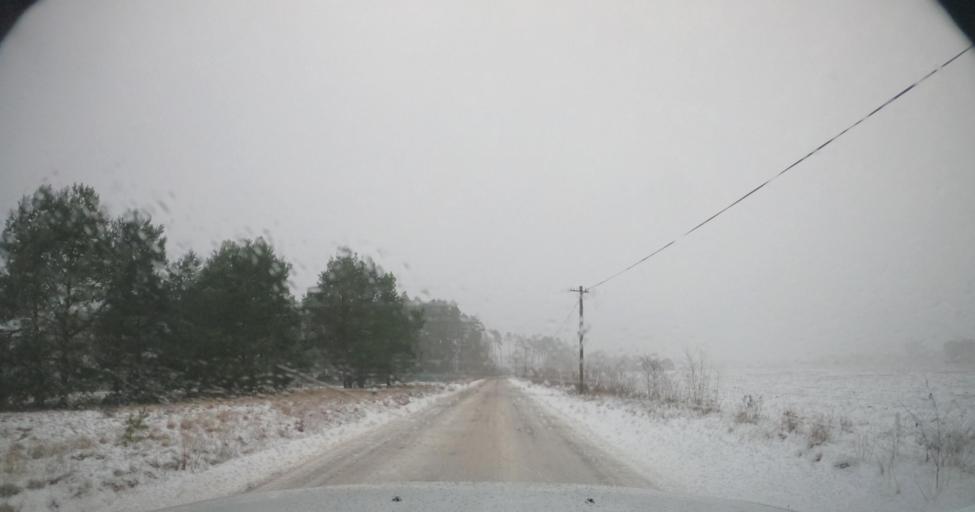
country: PL
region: West Pomeranian Voivodeship
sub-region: Powiat goleniowski
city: Przybiernow
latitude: 53.6869
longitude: 14.8446
